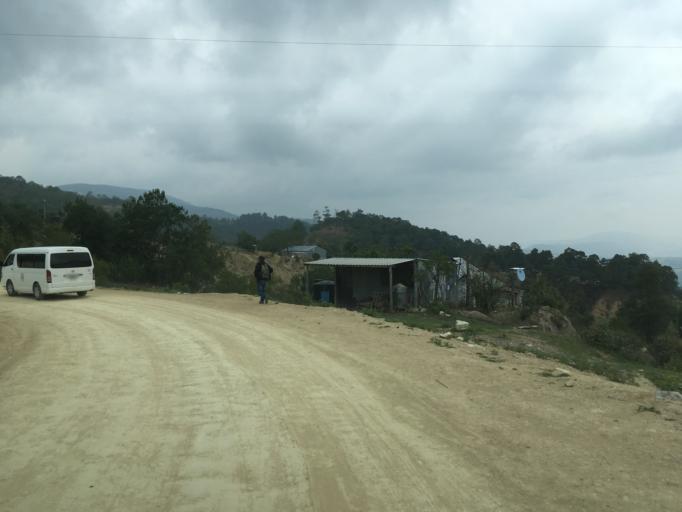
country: MX
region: Oaxaca
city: Santiago Tilantongo
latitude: 17.1976
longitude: -97.2818
